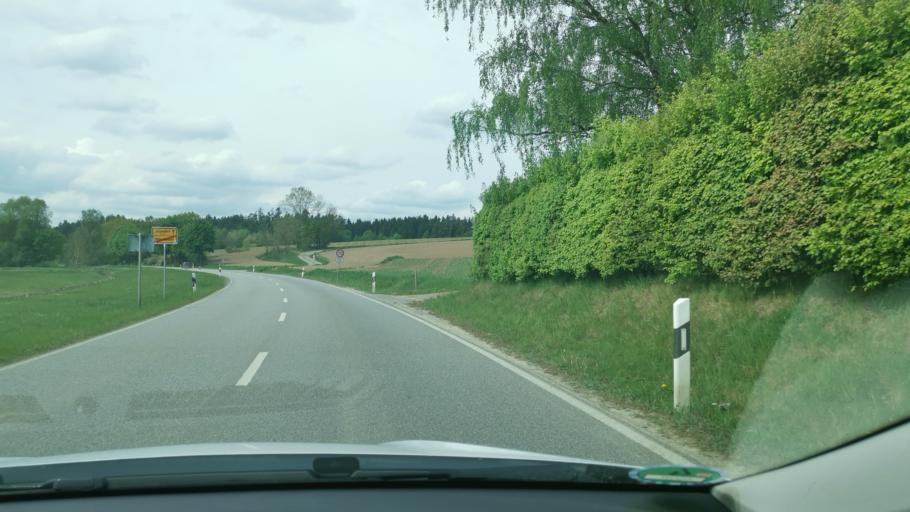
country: DE
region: Bavaria
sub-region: Upper Bavaria
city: Petershausen
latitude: 48.4127
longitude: 11.4623
